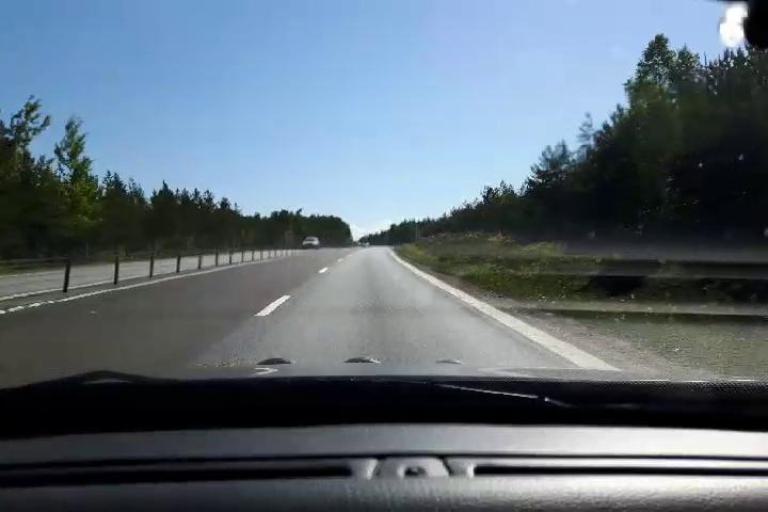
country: SE
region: Gaevleborg
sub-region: Gavle Kommun
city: Norrsundet
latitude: 60.9483
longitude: 17.0289
